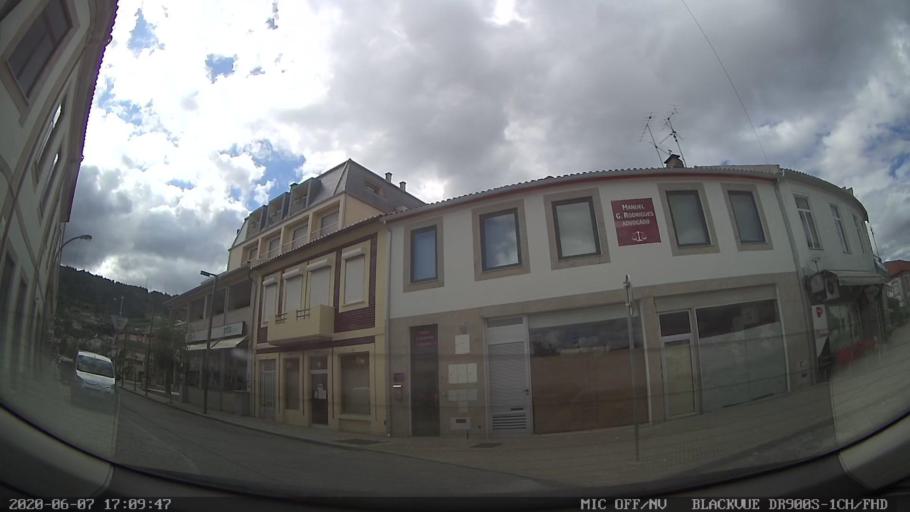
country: PT
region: Vila Real
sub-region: Vila Pouca de Aguiar
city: Vila Pouca de Aguiar
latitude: 41.5009
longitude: -7.6428
